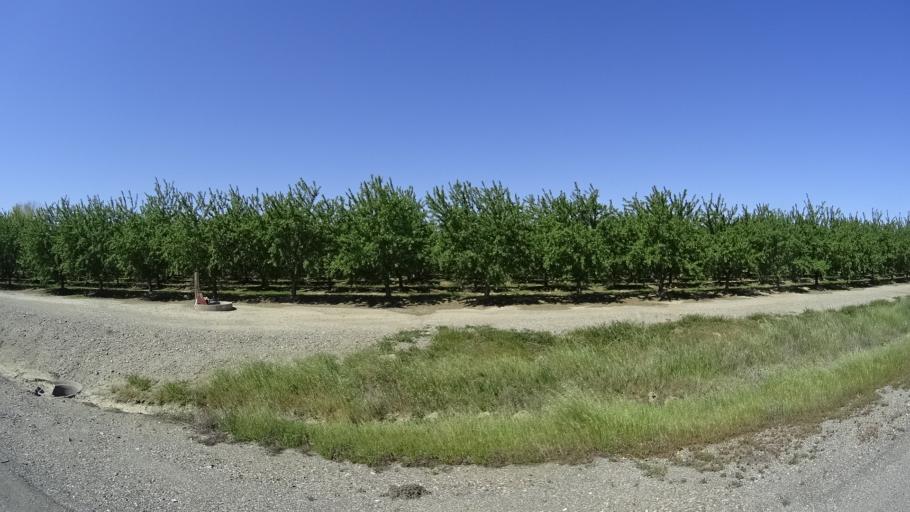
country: US
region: California
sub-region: Glenn County
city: Orland
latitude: 39.6942
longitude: -122.1220
